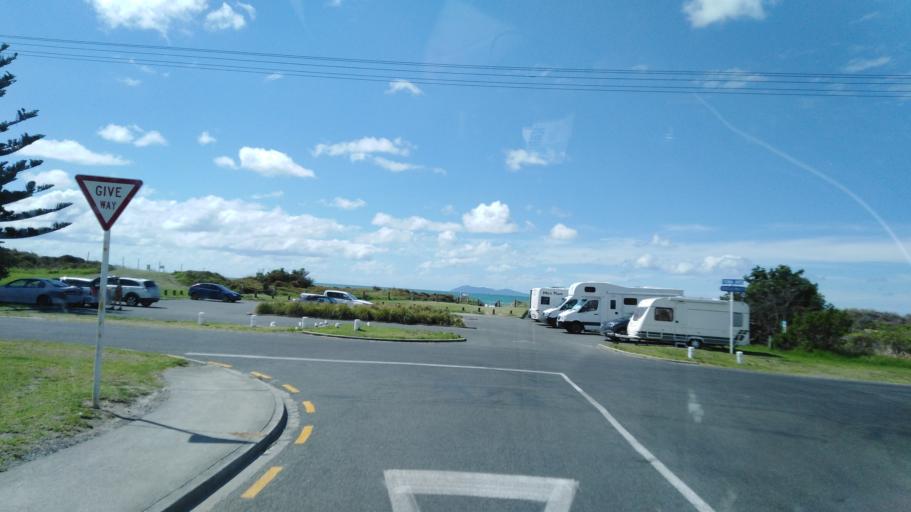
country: NZ
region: Bay of Plenty
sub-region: Western Bay of Plenty District
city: Waihi Beach
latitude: -37.4292
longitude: 175.9592
